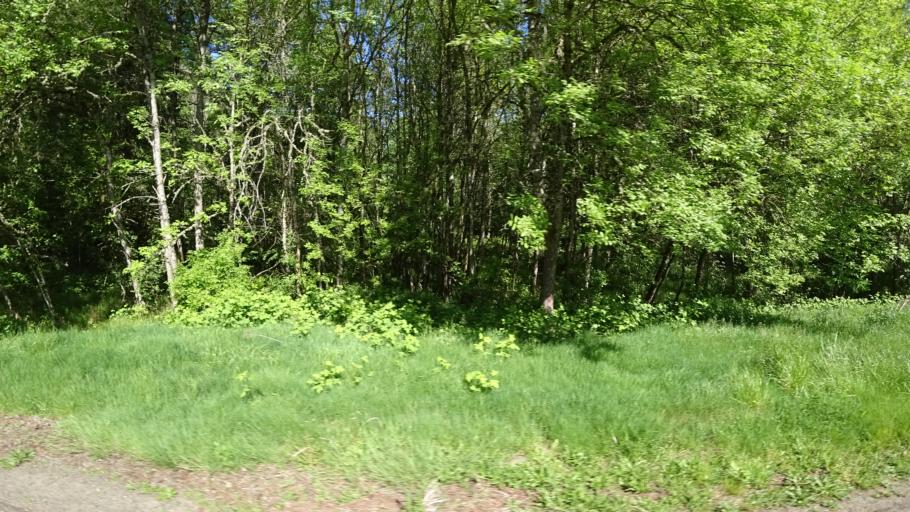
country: US
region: Oregon
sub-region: Washington County
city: Cedar Mill
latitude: 45.5535
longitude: -122.7960
